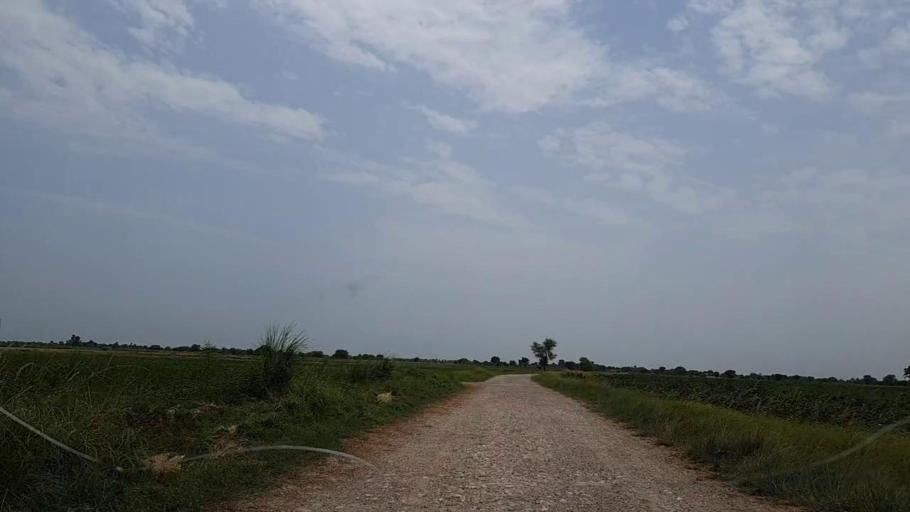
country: PK
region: Sindh
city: Tharu Shah
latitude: 26.9150
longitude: 68.0807
